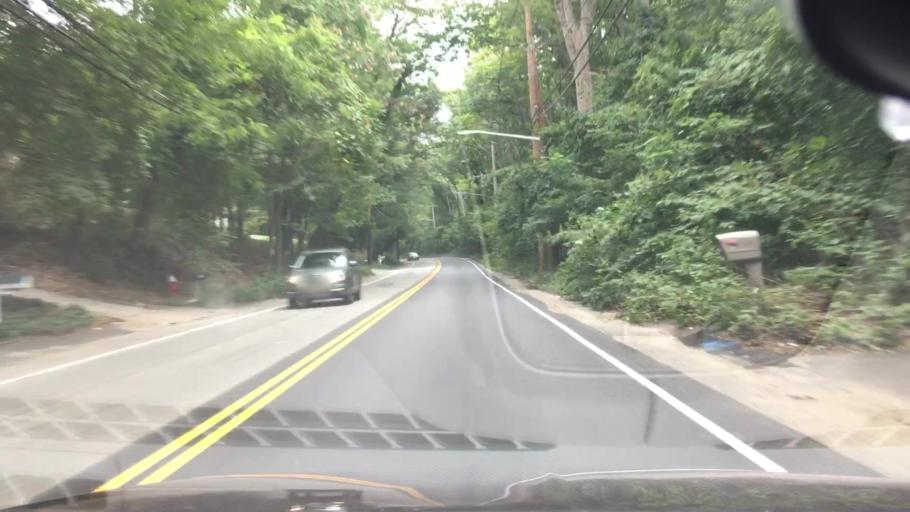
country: US
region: New York
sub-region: Suffolk County
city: Stony Brook
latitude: 40.9135
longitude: -73.1379
